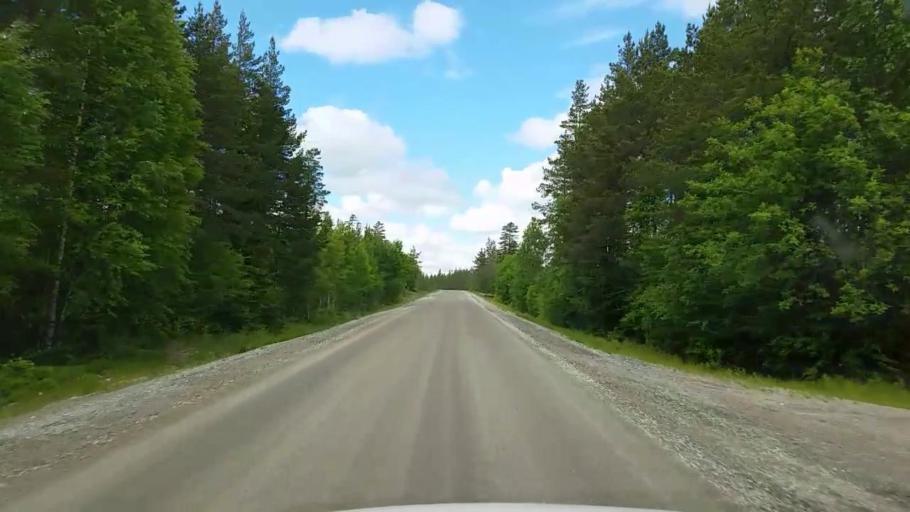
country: SE
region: Gaevleborg
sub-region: Bollnas Kommun
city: Kilafors
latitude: 61.0145
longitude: 16.3844
